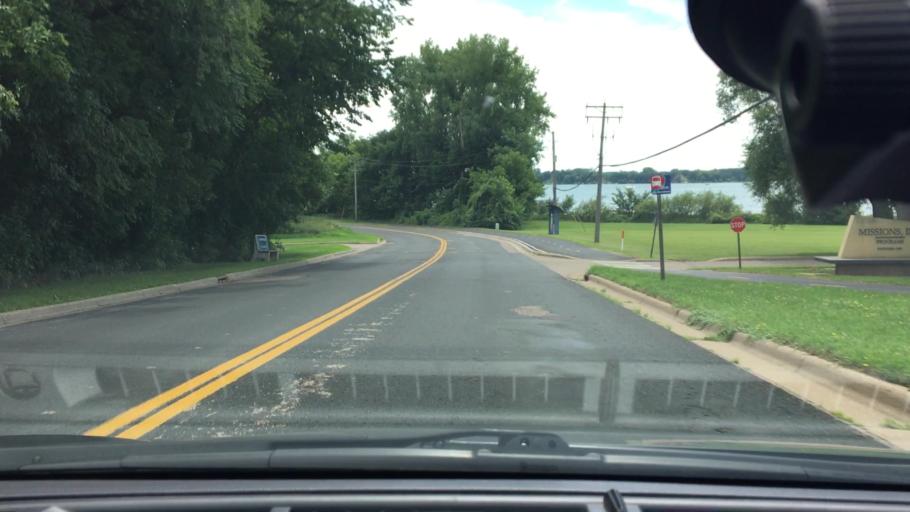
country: US
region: Minnesota
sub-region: Hennepin County
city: Plymouth
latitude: 45.0186
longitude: -93.4208
